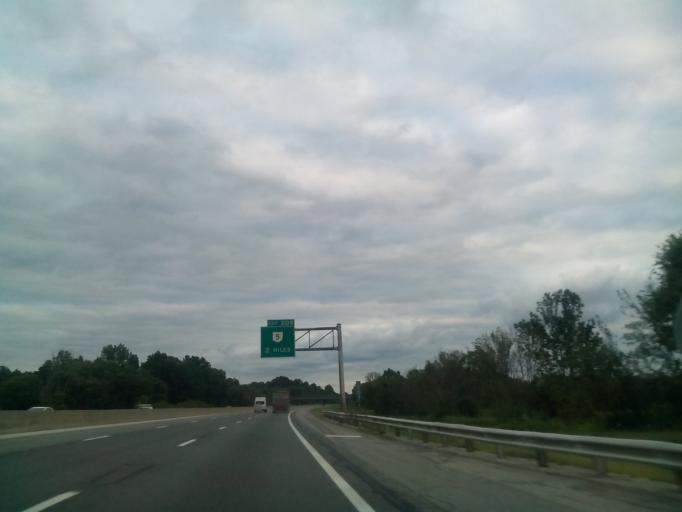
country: US
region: Ohio
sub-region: Trumbull County
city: Newton Falls
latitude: 41.2391
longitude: -80.9863
